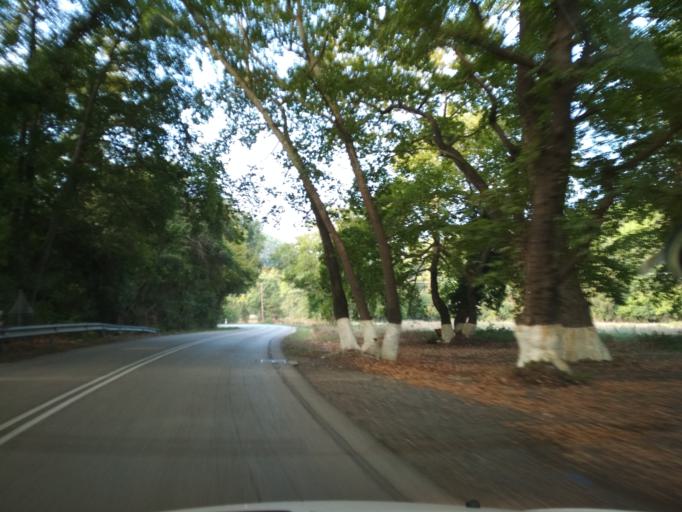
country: GR
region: Central Greece
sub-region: Nomos Evvoias
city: Mantoudi
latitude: 38.7698
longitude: 23.4767
